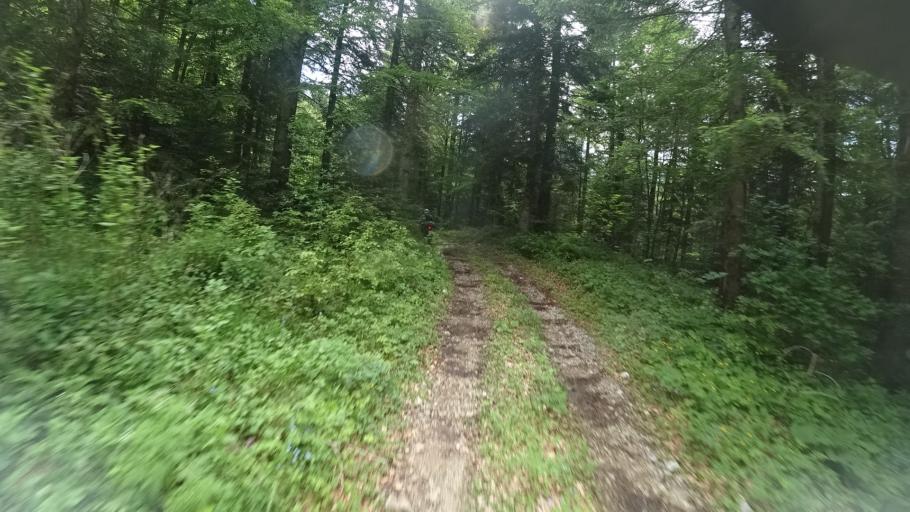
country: HR
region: Zadarska
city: Gracac
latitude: 44.4778
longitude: 15.8937
